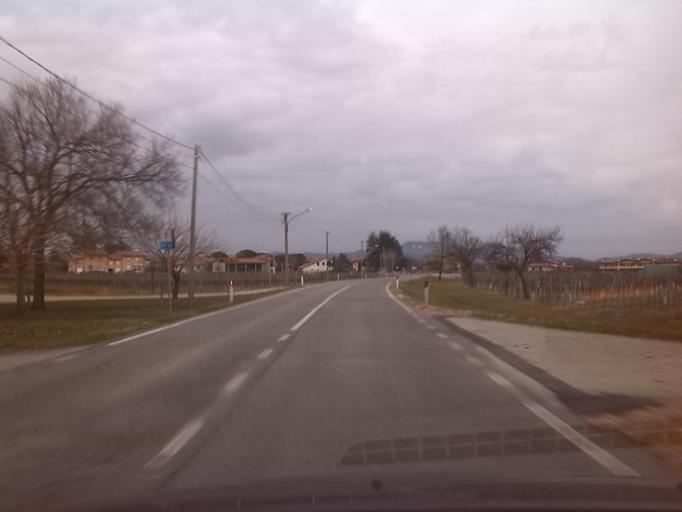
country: IT
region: Friuli Venezia Giulia
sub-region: Provincia di Gorizia
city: Mariano del Friuli
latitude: 45.9275
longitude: 13.4438
